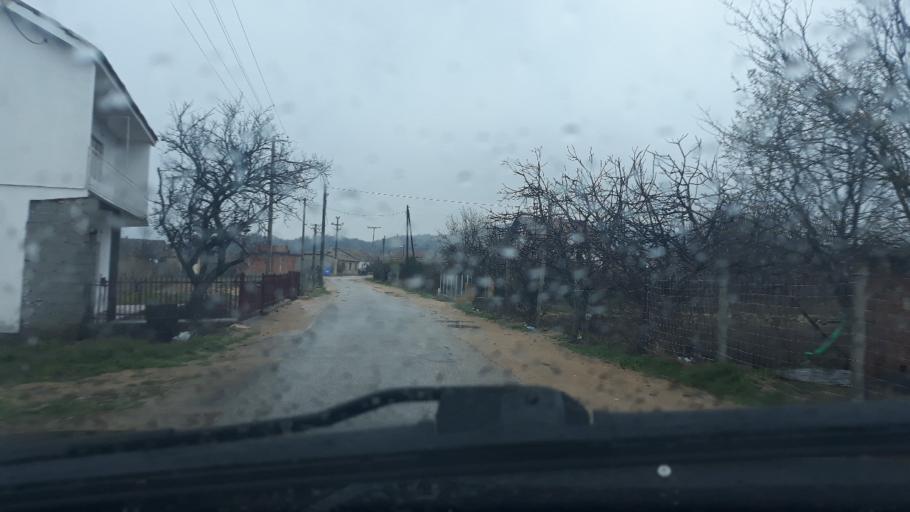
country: MK
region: Bogdanci
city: Bogdanci
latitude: 41.2444
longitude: 22.6123
